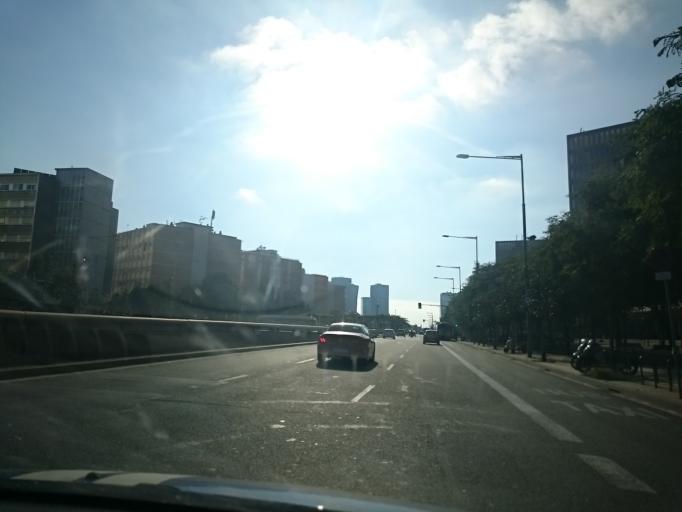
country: ES
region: Catalonia
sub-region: Provincia de Barcelona
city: Sants-Montjuic
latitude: 41.3643
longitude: 2.1345
